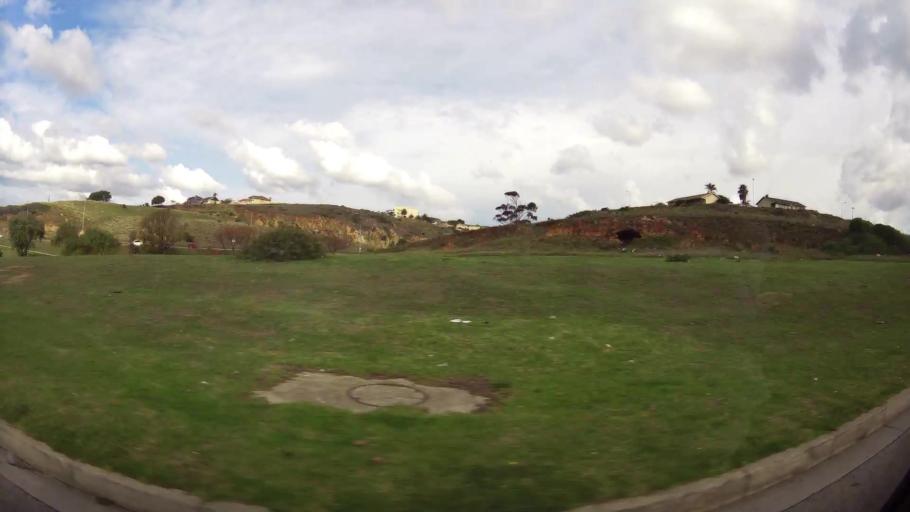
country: ZA
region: Eastern Cape
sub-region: Nelson Mandela Bay Metropolitan Municipality
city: Port Elizabeth
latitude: -33.9368
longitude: 25.5801
